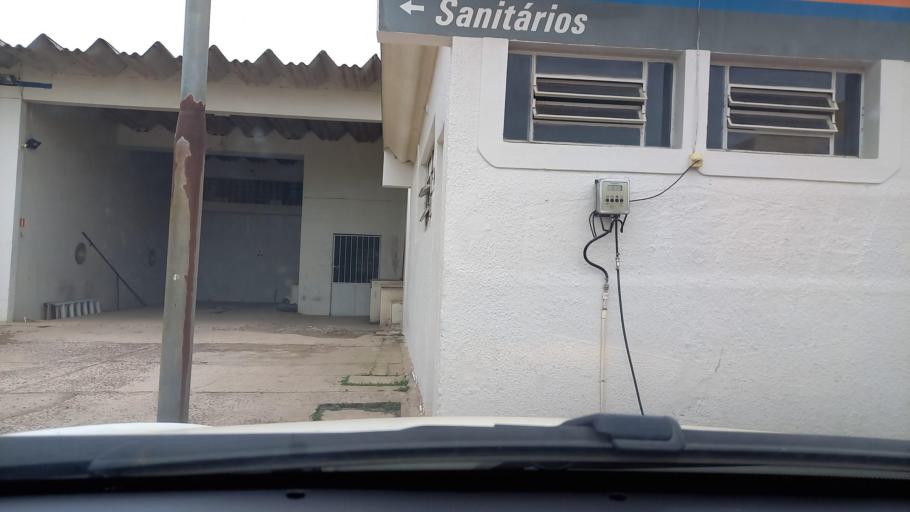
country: BR
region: Rio Grande do Sul
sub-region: Dom Pedrito
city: Dom Pedrito
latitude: -30.9807
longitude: -54.6665
